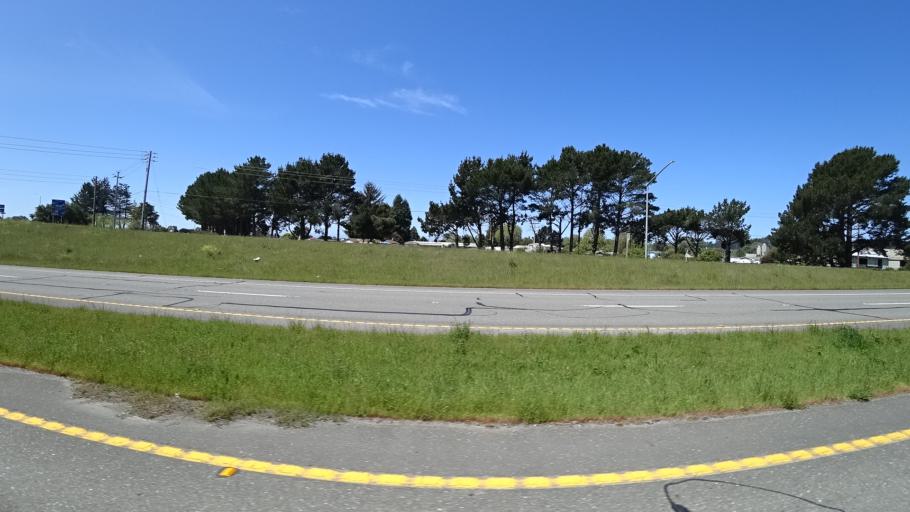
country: US
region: California
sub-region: Humboldt County
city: Arcata
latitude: 40.9057
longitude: -124.0732
